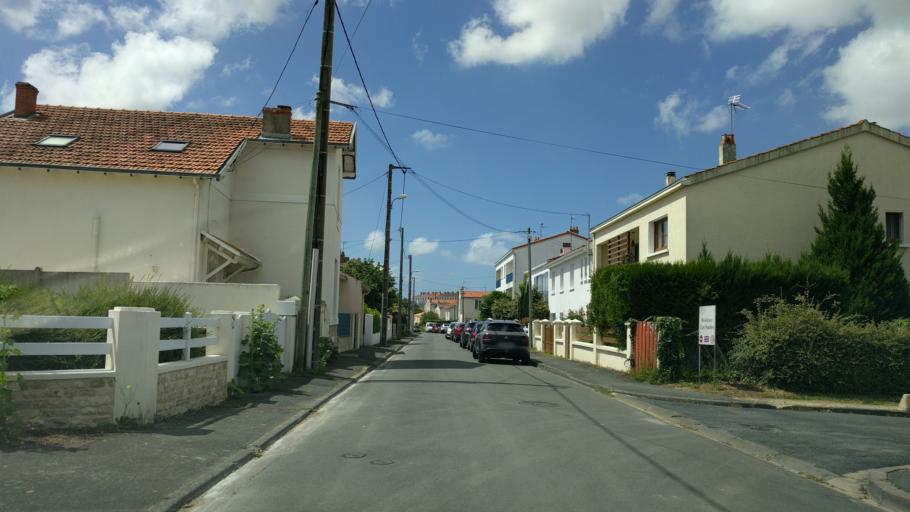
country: FR
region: Poitou-Charentes
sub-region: Departement de la Charente-Maritime
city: La Rochelle
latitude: 46.1724
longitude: -1.1432
